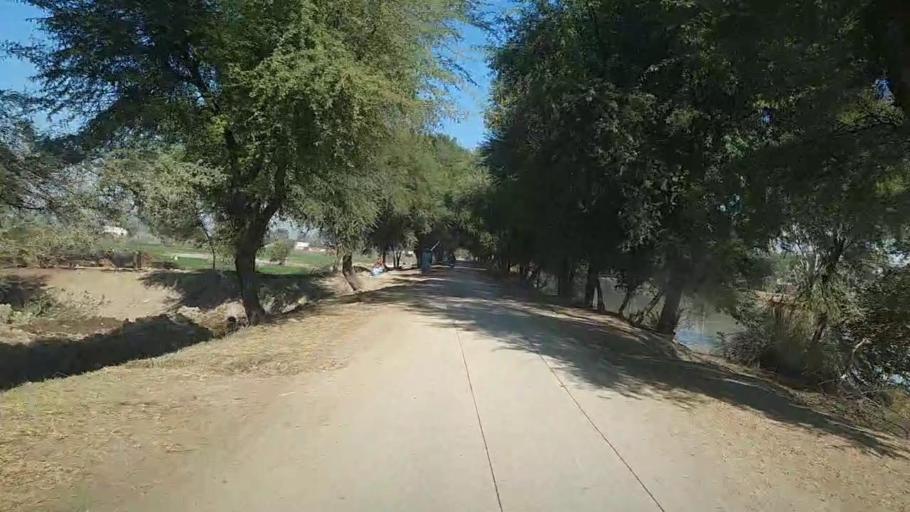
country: PK
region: Sindh
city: Khairpur
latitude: 28.0026
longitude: 69.6518
